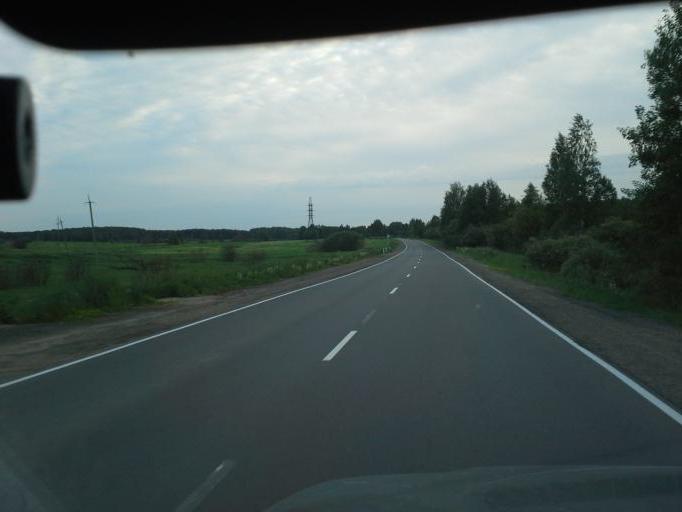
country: RU
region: Ivanovo
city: Petrovskiy
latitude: 56.6253
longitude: 40.2783
